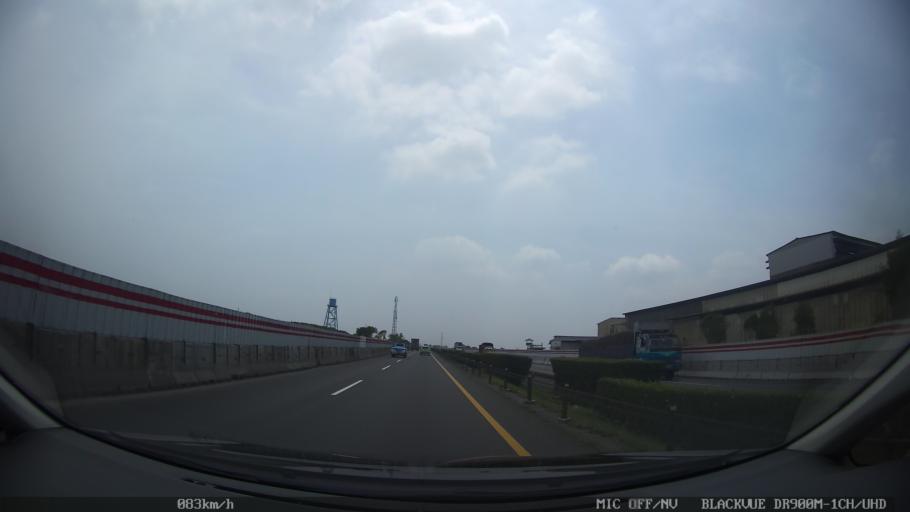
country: ID
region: West Java
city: Kresek
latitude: -6.1667
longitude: 106.3371
